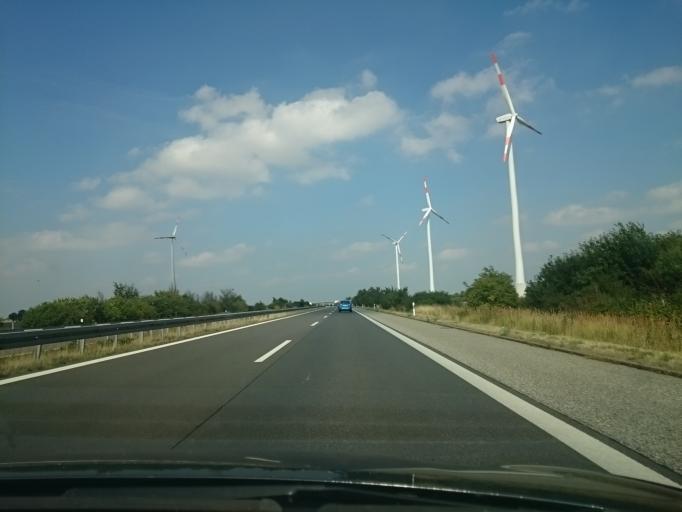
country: DE
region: Brandenburg
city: Schonfeld
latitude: 53.3828
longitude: 13.9887
